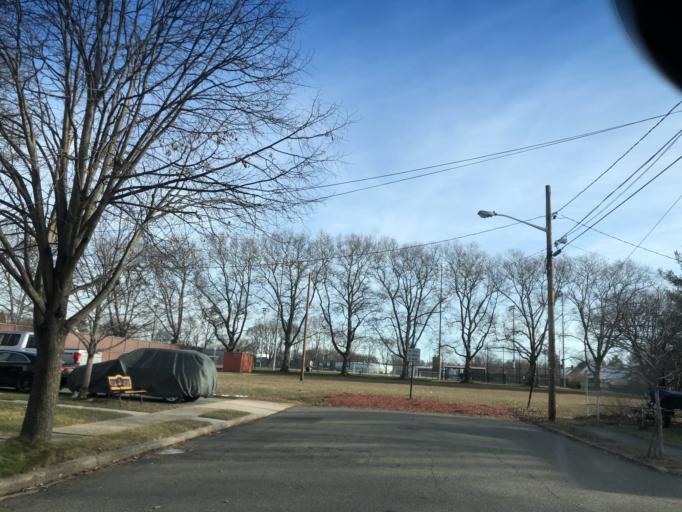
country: US
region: New Jersey
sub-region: Bergen County
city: Fair Lawn
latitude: 40.9302
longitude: -74.1250
